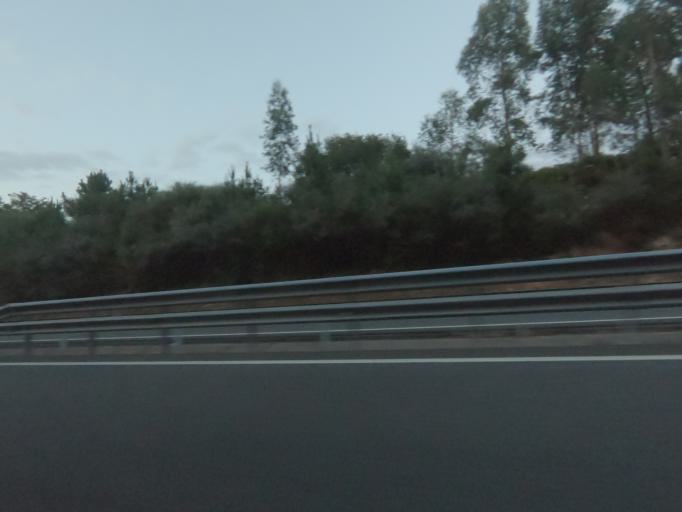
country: ES
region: Galicia
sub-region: Provincia de Pontevedra
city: Tui
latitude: 42.0730
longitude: -8.6318
